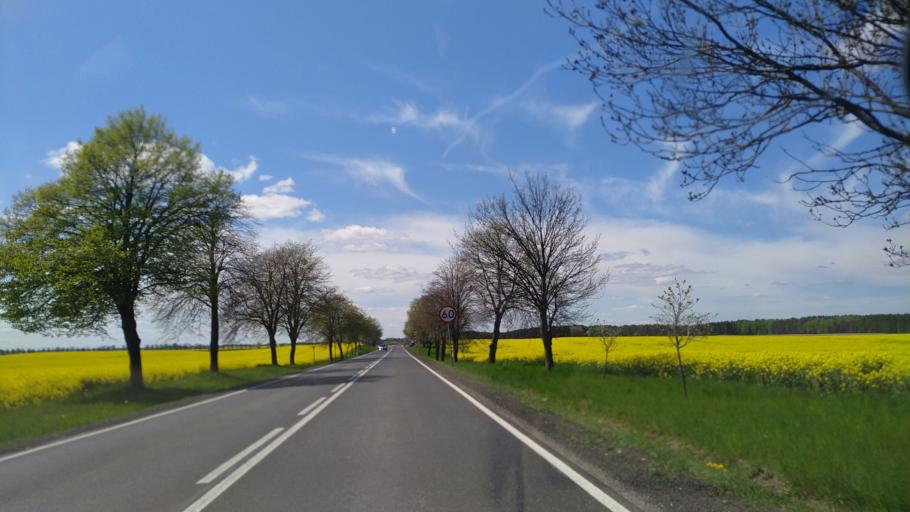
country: PL
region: Greater Poland Voivodeship
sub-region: Powiat pilski
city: Szydlowo
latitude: 53.2425
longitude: 16.6227
